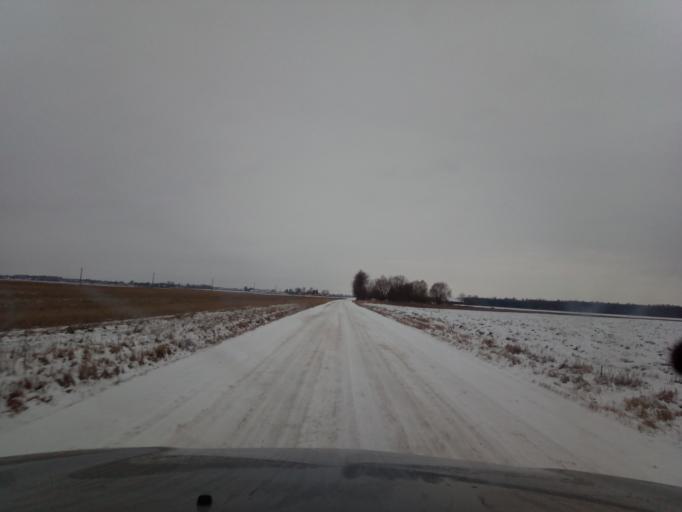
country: LT
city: Ramygala
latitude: 55.4942
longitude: 24.5411
